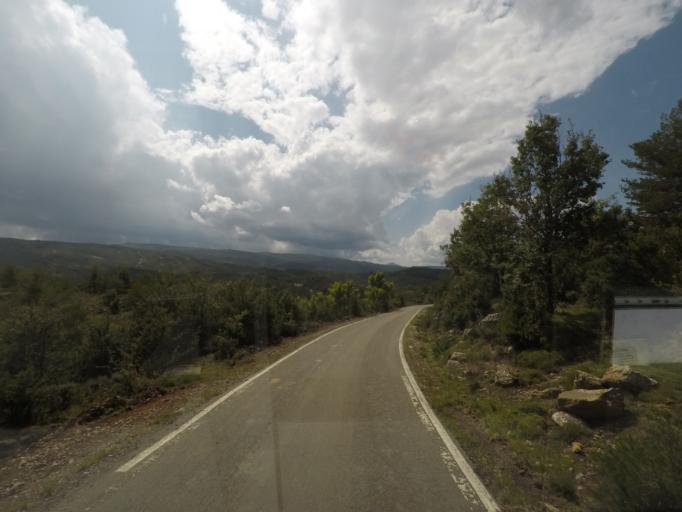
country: ES
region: Aragon
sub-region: Provincia de Huesca
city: Fiscal
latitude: 42.4090
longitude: -0.1324
